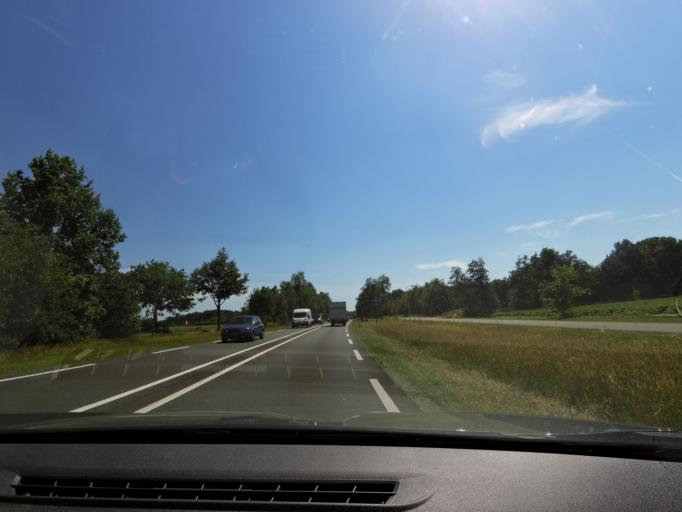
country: NL
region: Gelderland
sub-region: Oost Gelre
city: Lichtenvoorde
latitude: 52.0223
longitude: 6.6157
